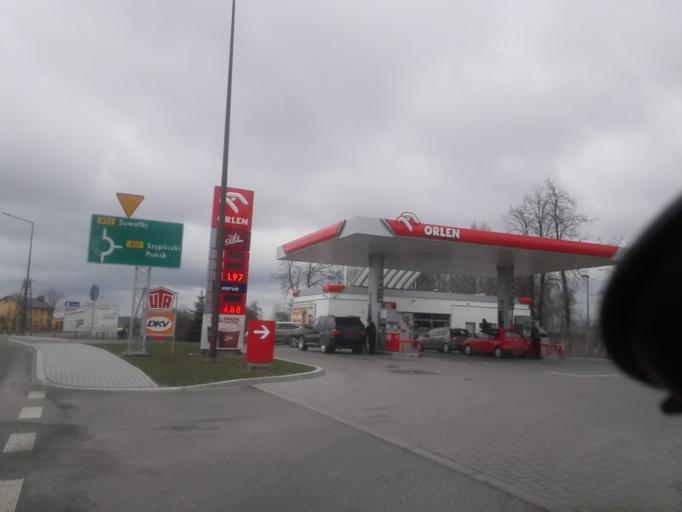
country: PL
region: Podlasie
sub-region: Powiat sejnenski
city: Sejny
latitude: 54.1091
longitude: 23.3374
